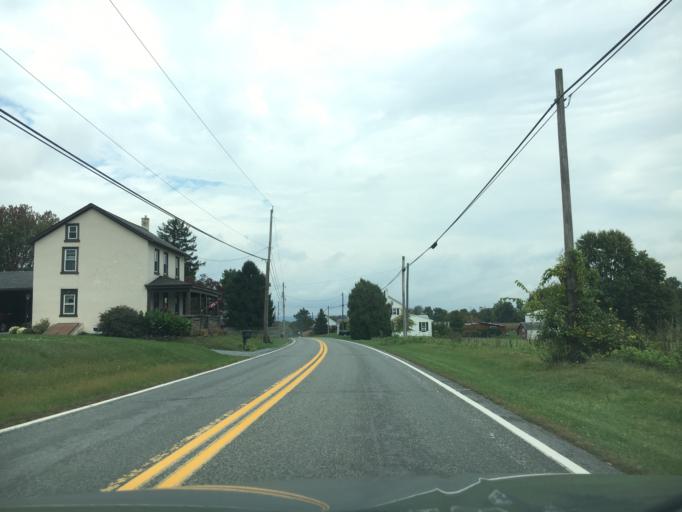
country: US
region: Pennsylvania
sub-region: Berks County
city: Topton
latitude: 40.4520
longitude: -75.7469
